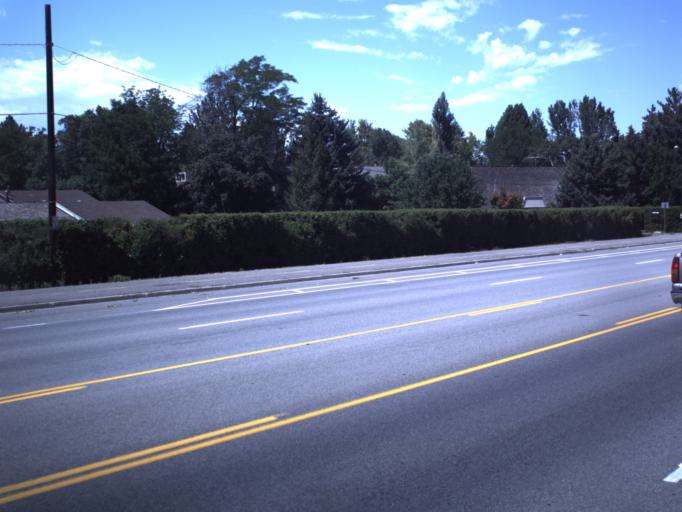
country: US
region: Utah
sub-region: Utah County
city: Provo
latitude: 40.2712
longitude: -111.6569
